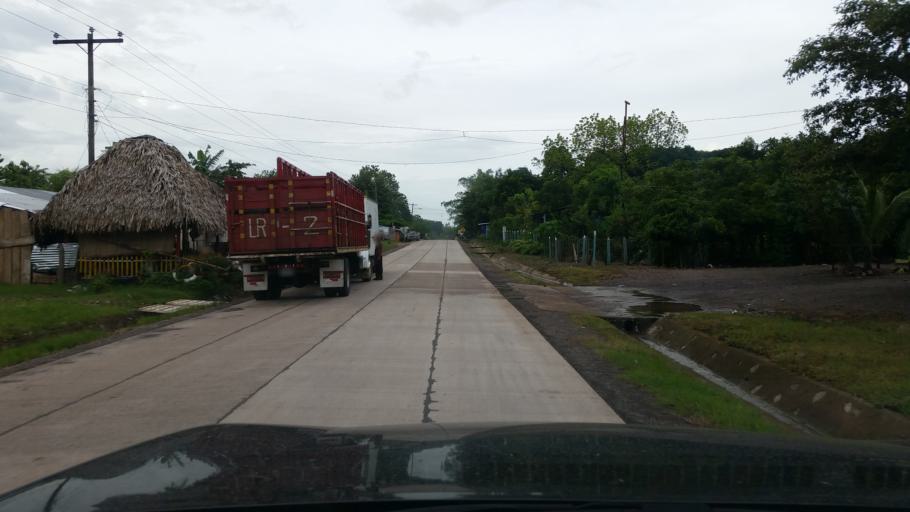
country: NI
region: Matagalpa
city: Rio Blanco
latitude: 13.1611
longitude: -84.9685
